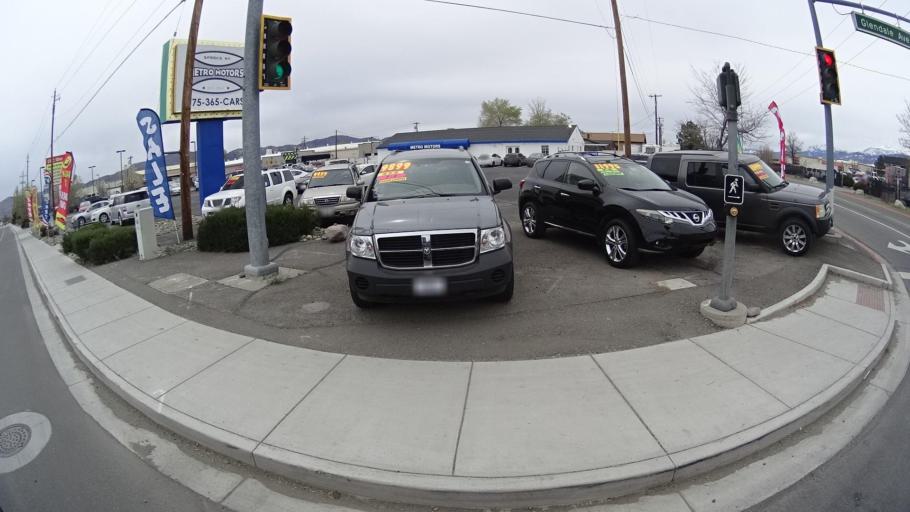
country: US
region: Nevada
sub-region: Washoe County
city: Sparks
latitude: 39.5275
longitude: -119.7714
